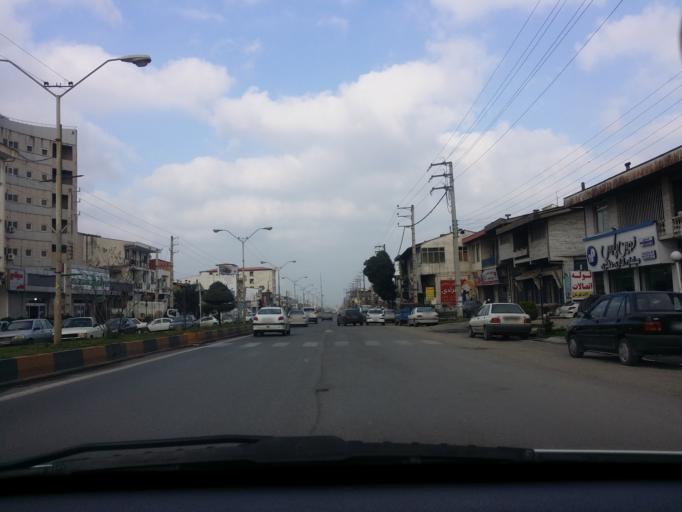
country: IR
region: Mazandaran
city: Chalus
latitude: 36.6670
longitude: 51.4097
